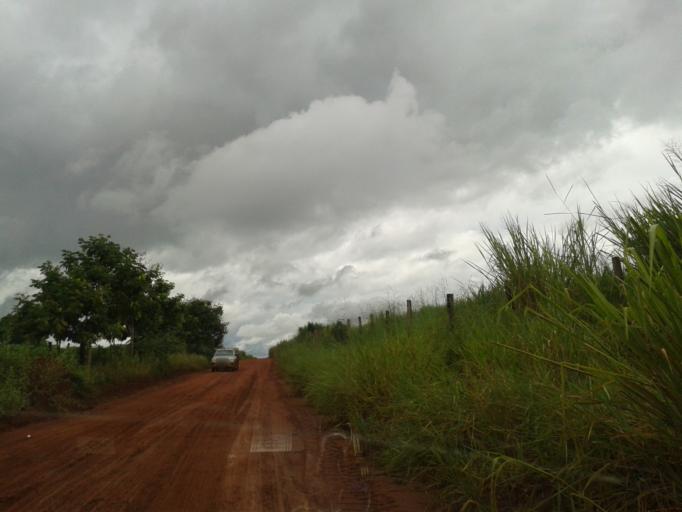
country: BR
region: Minas Gerais
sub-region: Santa Vitoria
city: Santa Vitoria
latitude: -18.6850
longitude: -49.9395
